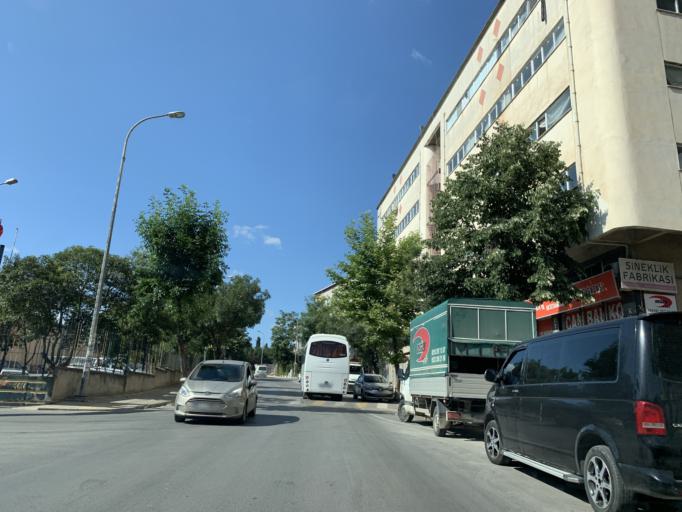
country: TR
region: Istanbul
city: Pendik
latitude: 40.8845
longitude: 29.2831
